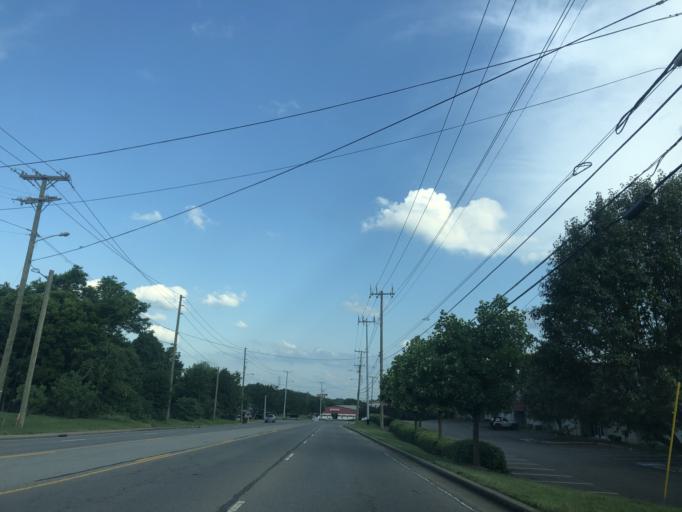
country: US
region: Tennessee
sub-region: Davidson County
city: Nashville
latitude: 36.2165
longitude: -86.7810
